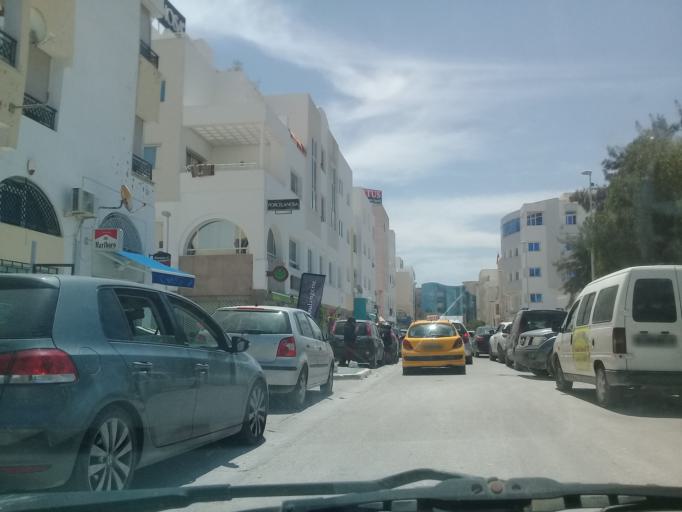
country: TN
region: Ariana
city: Ariana
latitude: 36.8370
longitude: 10.2464
